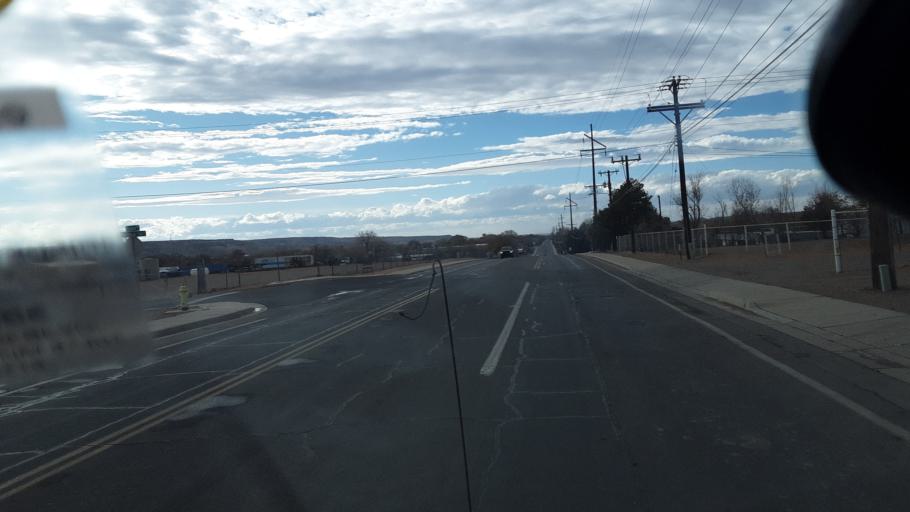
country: US
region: New Mexico
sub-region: San Juan County
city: Farmington
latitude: 36.7264
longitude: -108.1643
